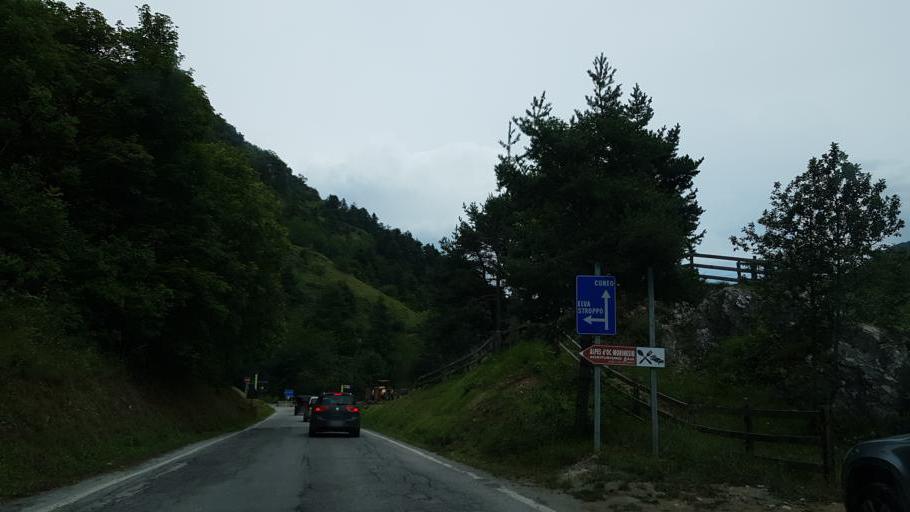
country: IT
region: Piedmont
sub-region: Provincia di Cuneo
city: Stroppo
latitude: 44.5030
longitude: 7.1341
